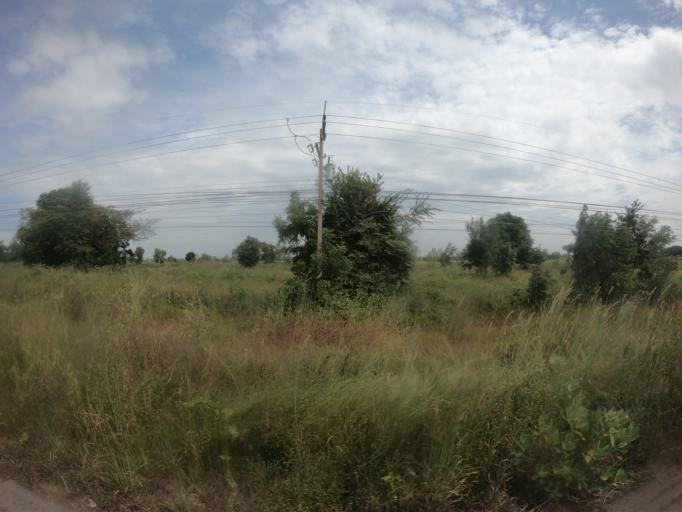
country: TH
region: Maha Sarakham
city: Chiang Yuen
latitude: 16.3588
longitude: 103.1125
